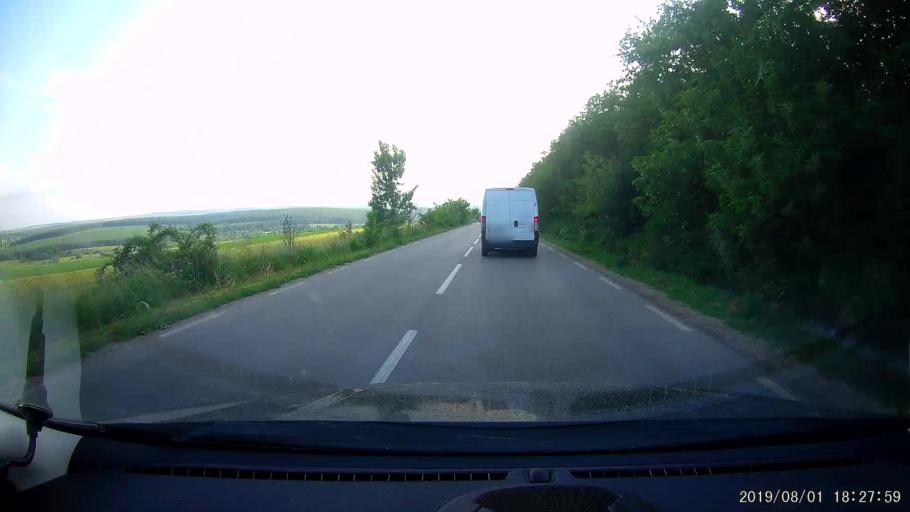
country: BG
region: Shumen
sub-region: Obshtina Venets
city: Venets
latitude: 43.5798
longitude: 26.9730
